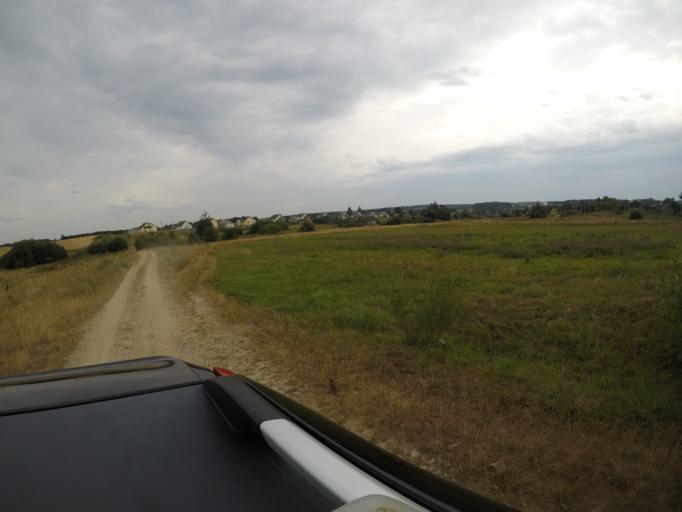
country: BY
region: Grodnenskaya
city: Hal'shany
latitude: 54.2587
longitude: 26.0239
